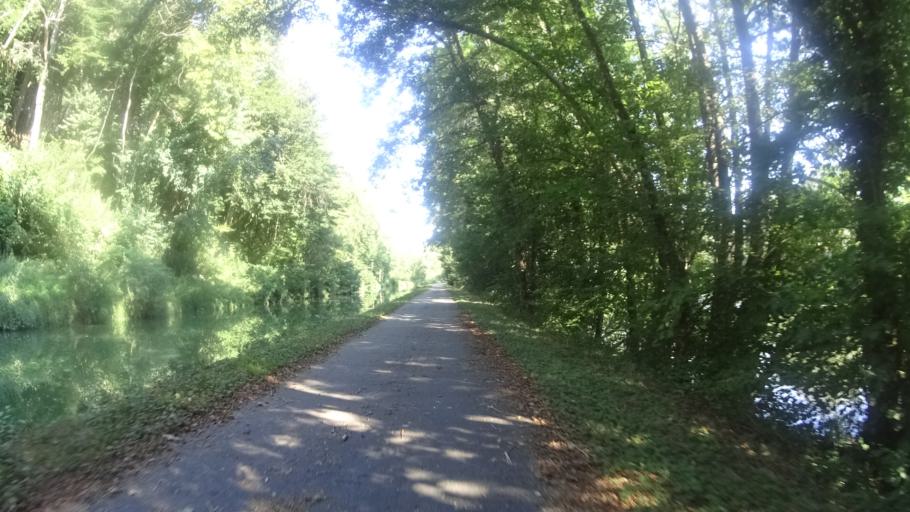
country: FR
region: Franche-Comte
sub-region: Departement du Doubs
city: Montenois
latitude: 47.4354
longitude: 6.5994
